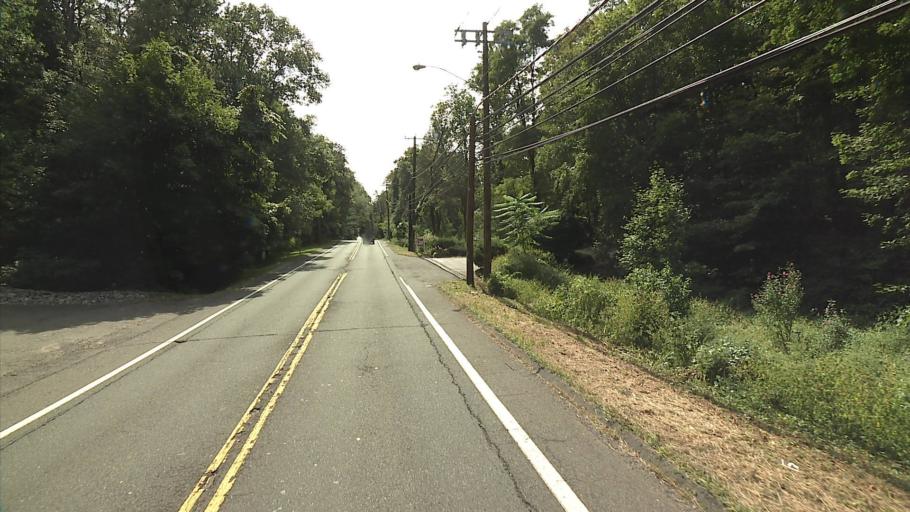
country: US
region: Connecticut
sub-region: Fairfield County
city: North Stamford
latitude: 41.1105
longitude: -73.5707
